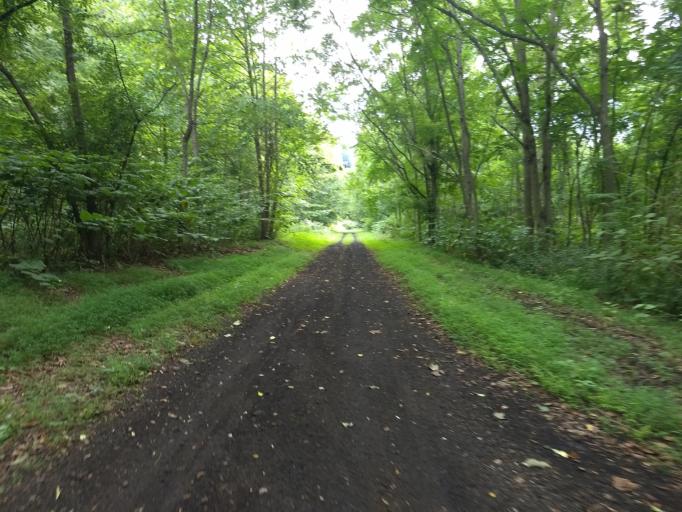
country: US
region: Pennsylvania
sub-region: Armstrong County
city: Freeport
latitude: 40.6724
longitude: -79.6720
